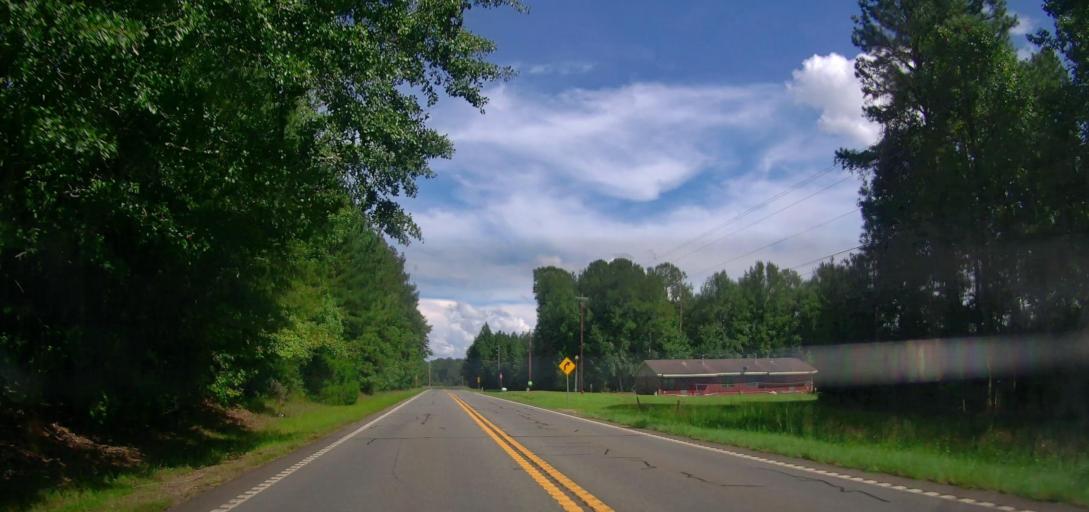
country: US
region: Georgia
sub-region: Talbot County
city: Sardis
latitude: 32.7980
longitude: -84.5744
